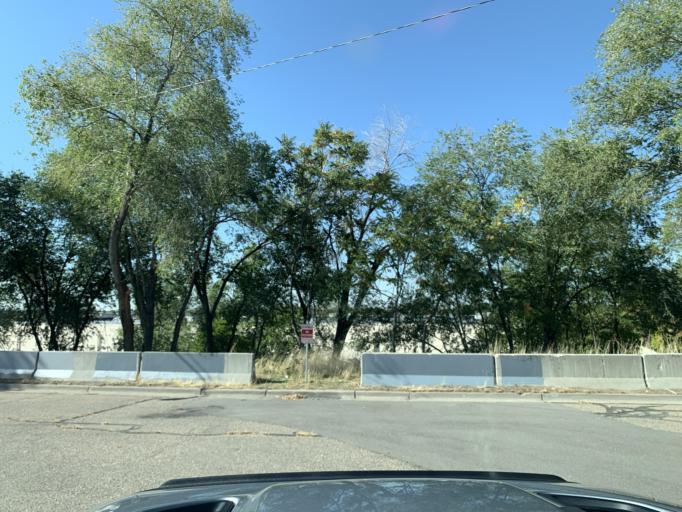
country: US
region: Utah
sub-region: Weber County
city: Ogden
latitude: 41.2478
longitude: -111.9739
